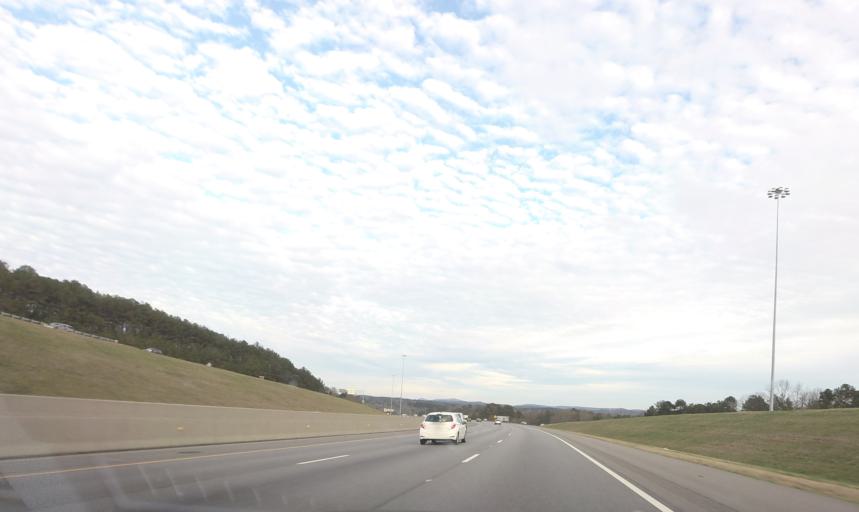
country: US
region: Alabama
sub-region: Jefferson County
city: Irondale
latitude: 33.5446
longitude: -86.6410
